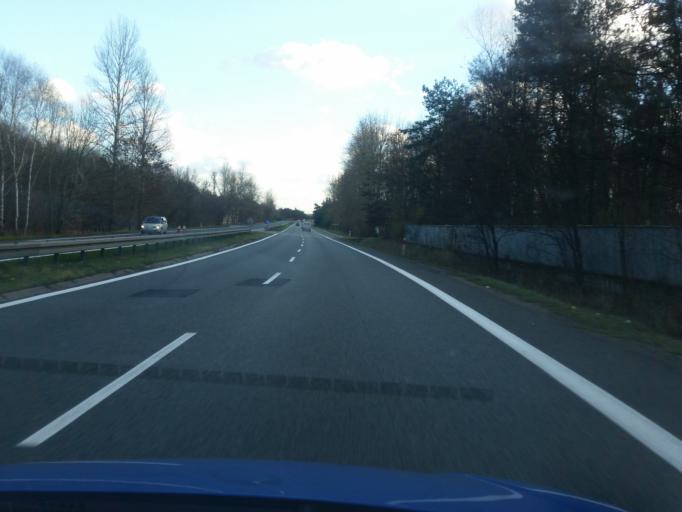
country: PL
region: Silesian Voivodeship
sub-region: Powiat bedzinski
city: Siewierz
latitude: 50.4846
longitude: 19.2183
